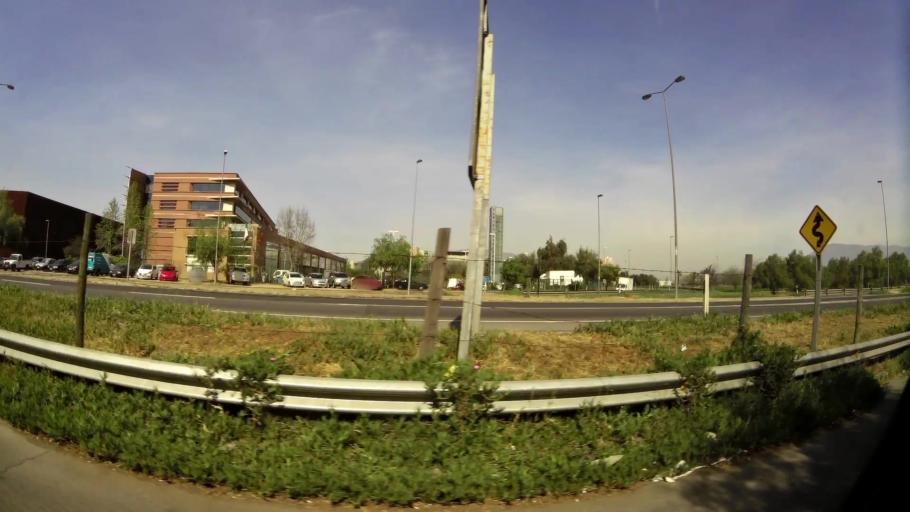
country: CL
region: Santiago Metropolitan
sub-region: Provincia de Santiago
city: Lo Prado
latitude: -33.4267
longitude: -70.7802
